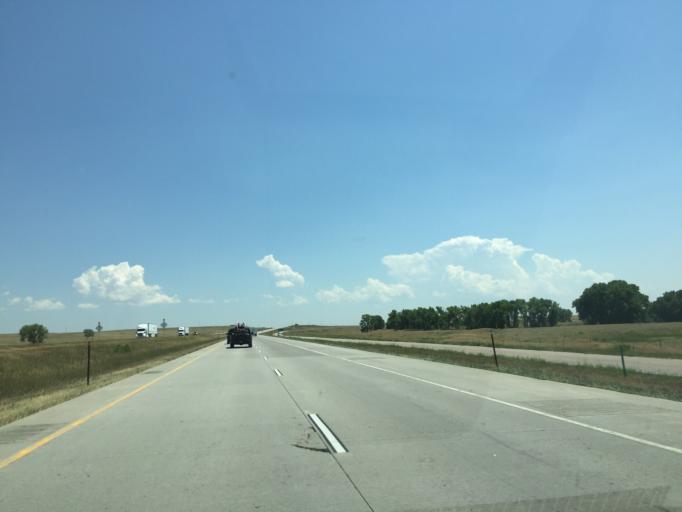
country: US
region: Colorado
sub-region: Arapahoe County
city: Byers
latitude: 39.4949
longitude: -103.9630
